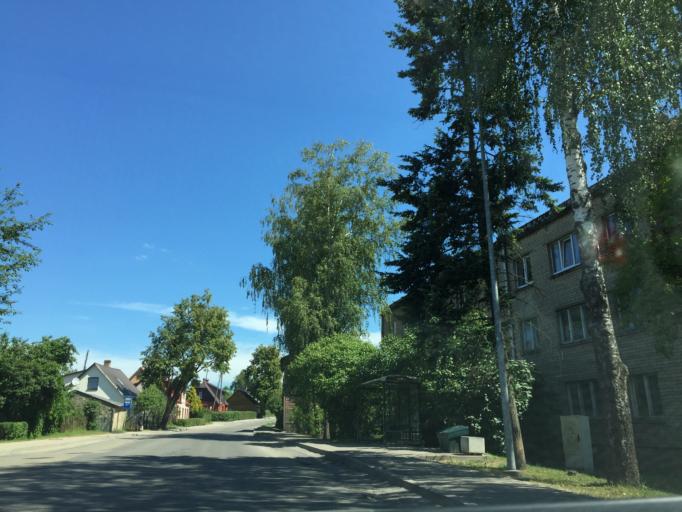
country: LV
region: Jekabpils Rajons
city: Jekabpils
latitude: 56.5026
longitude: 25.8814
